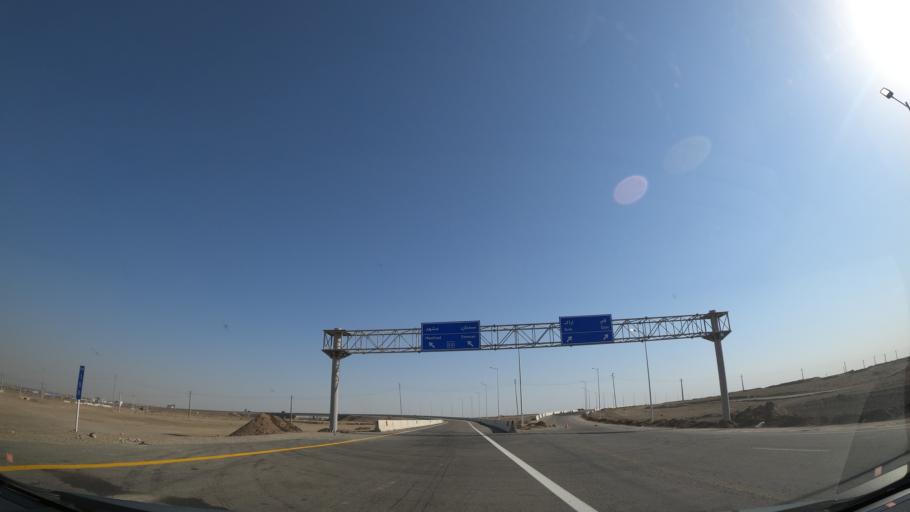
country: IR
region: Tehran
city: Eqbaliyeh
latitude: 35.1360
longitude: 51.5077
